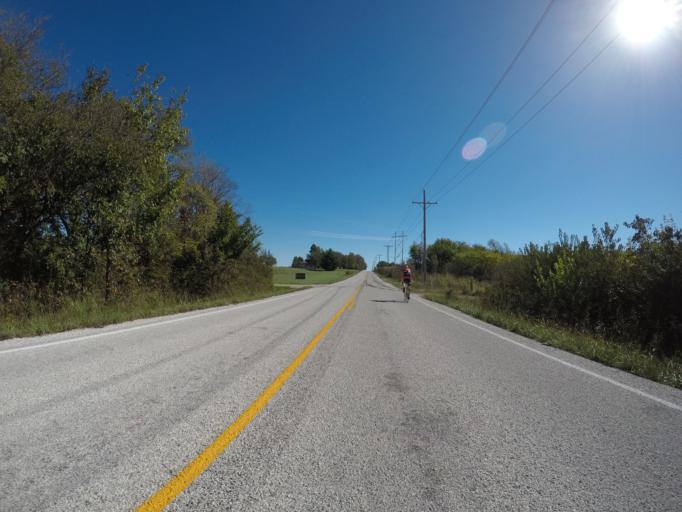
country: US
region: Kansas
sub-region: Leavenworth County
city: Basehor
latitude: 39.1017
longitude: -94.9548
